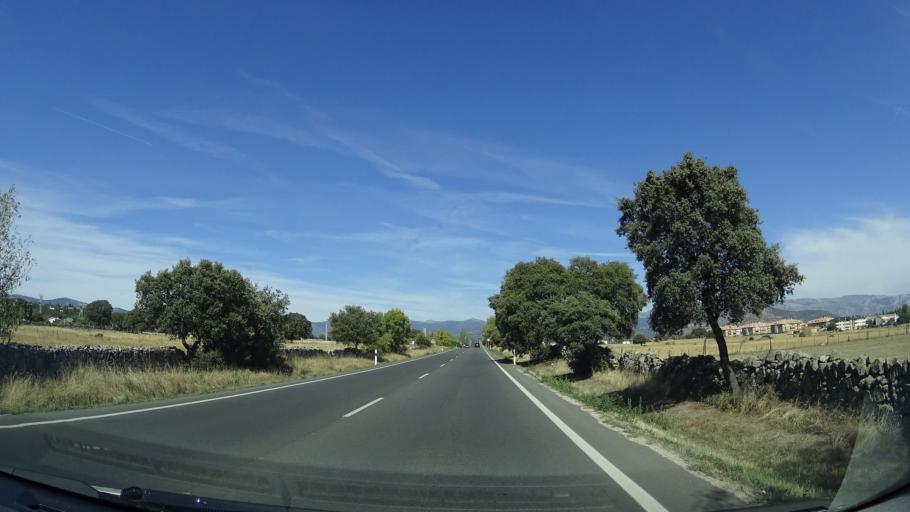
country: ES
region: Madrid
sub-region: Provincia de Madrid
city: Navalquejigo
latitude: 40.6160
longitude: -4.0243
